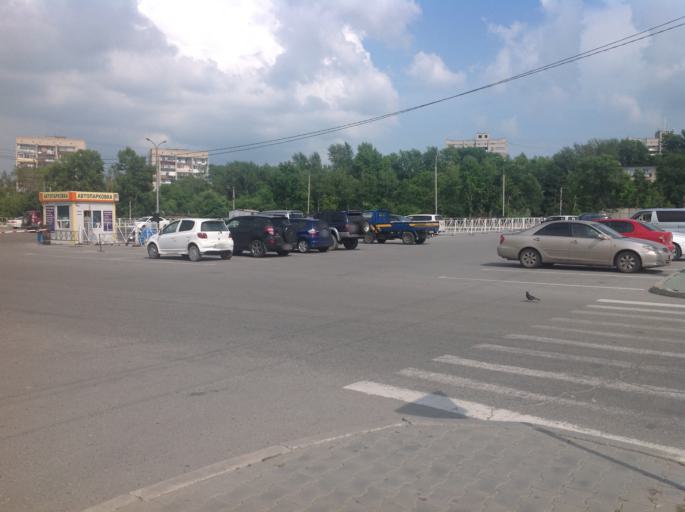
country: RU
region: Khabarovsk Krai
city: Khabarovsk Vtoroy
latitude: 48.3949
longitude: 135.1066
